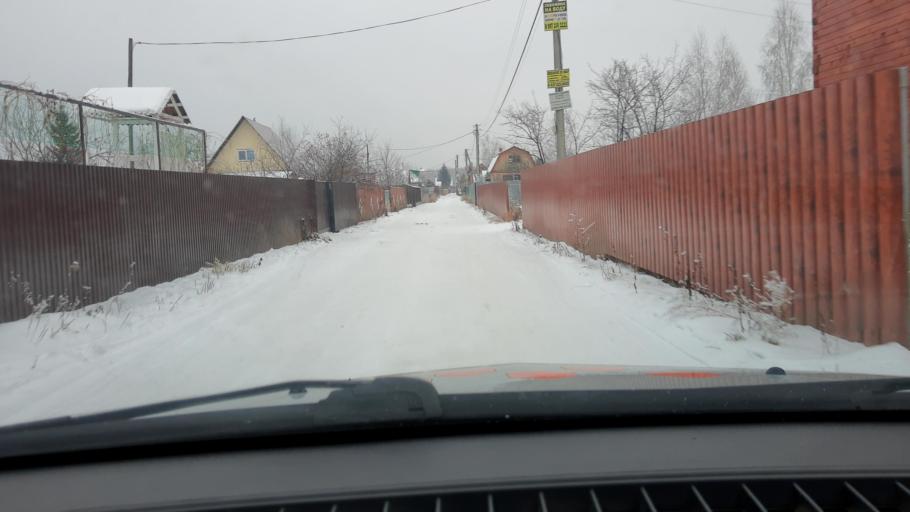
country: RU
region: Bashkortostan
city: Iglino
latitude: 54.8339
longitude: 56.2246
